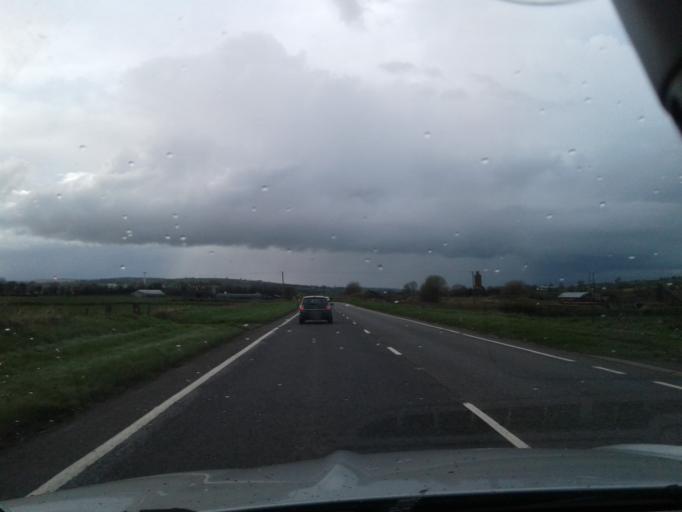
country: GB
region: Northern Ireland
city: Newtownstewart
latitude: 54.7278
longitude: -7.4086
